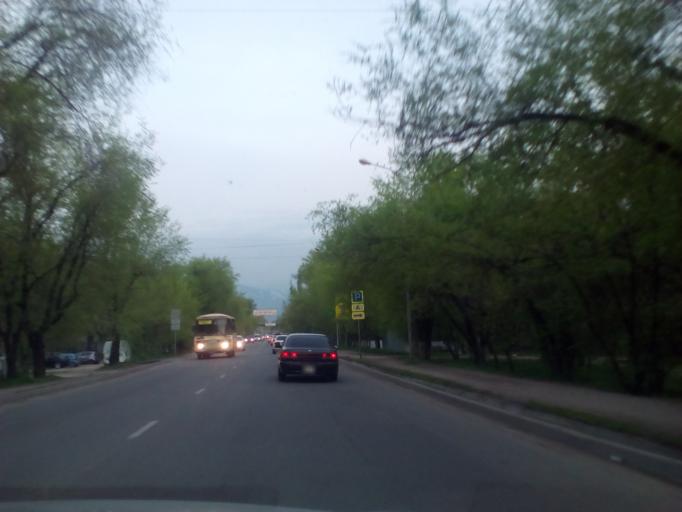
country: KZ
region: Almaty Qalasy
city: Almaty
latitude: 43.2364
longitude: 76.8243
